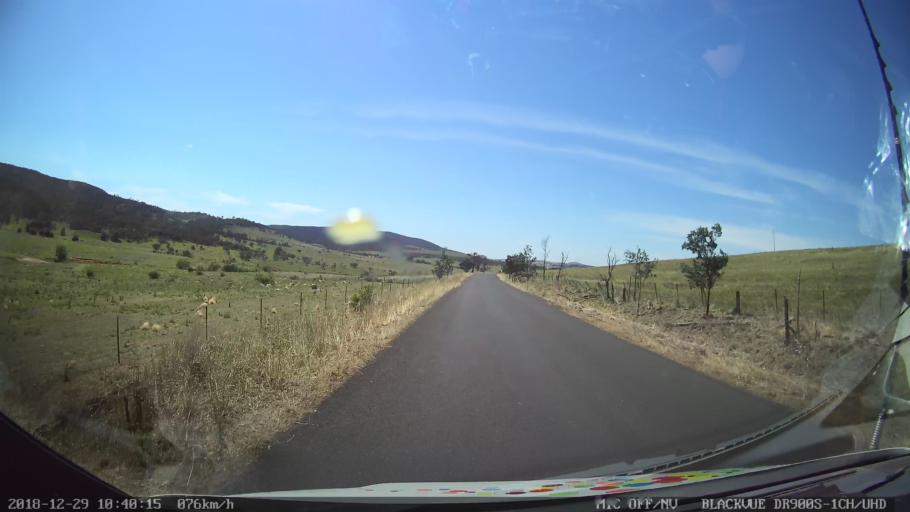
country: AU
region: New South Wales
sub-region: Palerang
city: Bungendore
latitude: -35.0137
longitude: 149.5168
